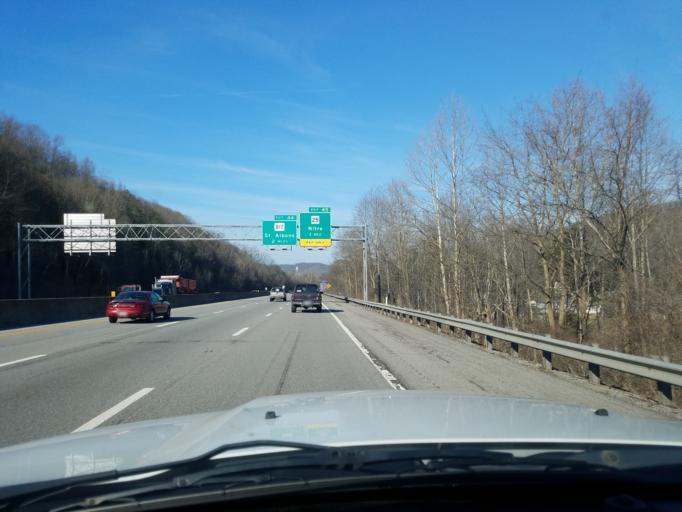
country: US
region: West Virginia
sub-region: Kanawha County
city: Cross Lanes
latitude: 38.4274
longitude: -81.8168
